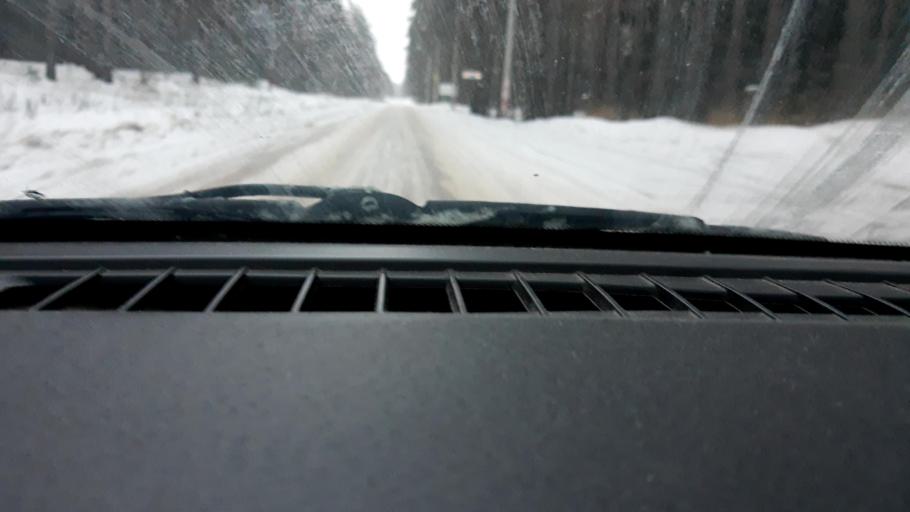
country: RU
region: Nizjnij Novgorod
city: Afonino
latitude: 56.1738
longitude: 44.0846
